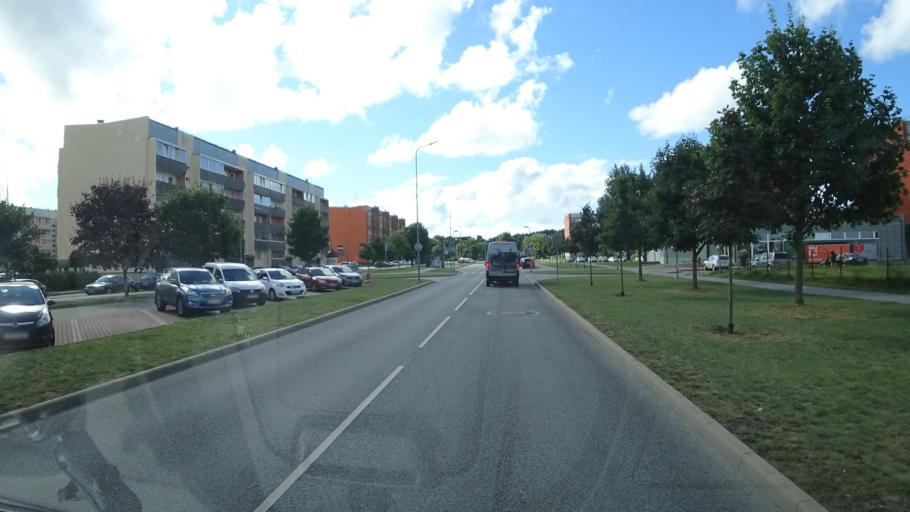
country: LV
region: Ventspils
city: Ventspils
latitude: 57.4077
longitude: 21.5980
